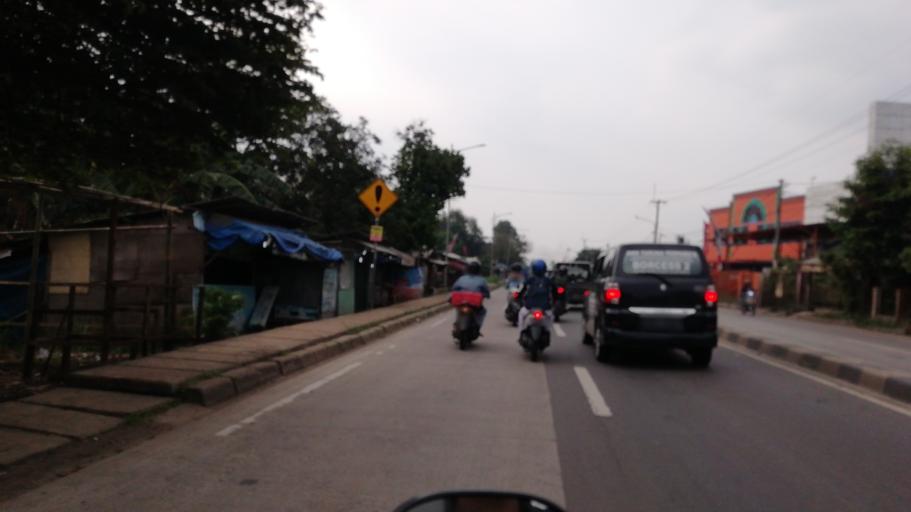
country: ID
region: West Java
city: Ciampea
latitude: -6.4974
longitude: 106.7547
